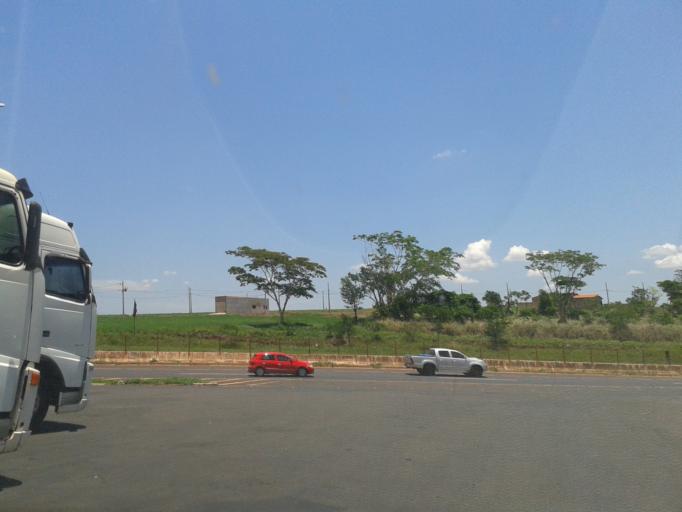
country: BR
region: Goias
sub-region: Itumbiara
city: Itumbiara
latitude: -18.4253
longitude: -49.1933
